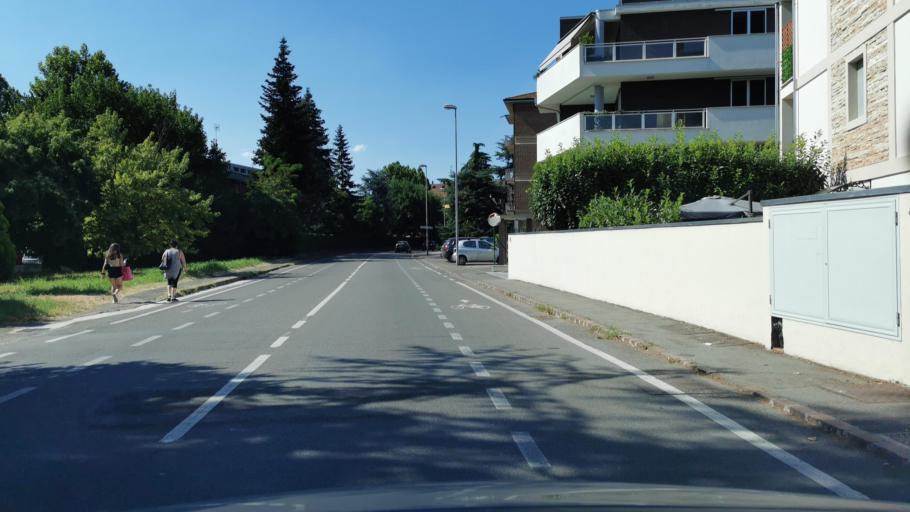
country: IT
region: Emilia-Romagna
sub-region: Provincia di Modena
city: Modena
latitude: 44.6231
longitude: 10.9276
